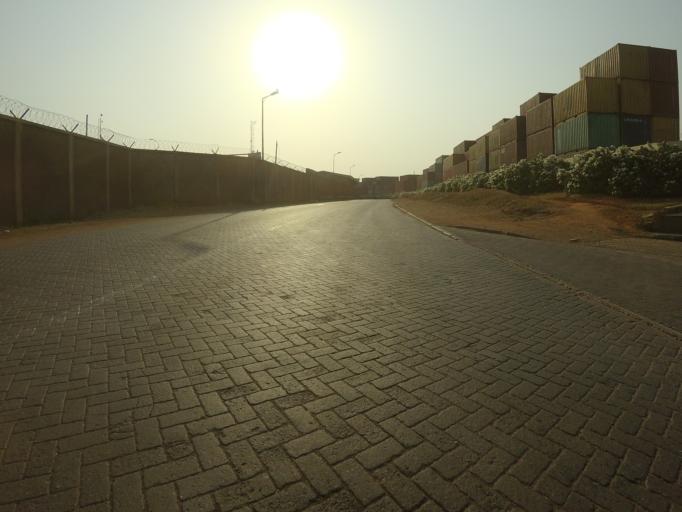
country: GH
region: Greater Accra
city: Tema
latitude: 5.6254
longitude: -0.0047
